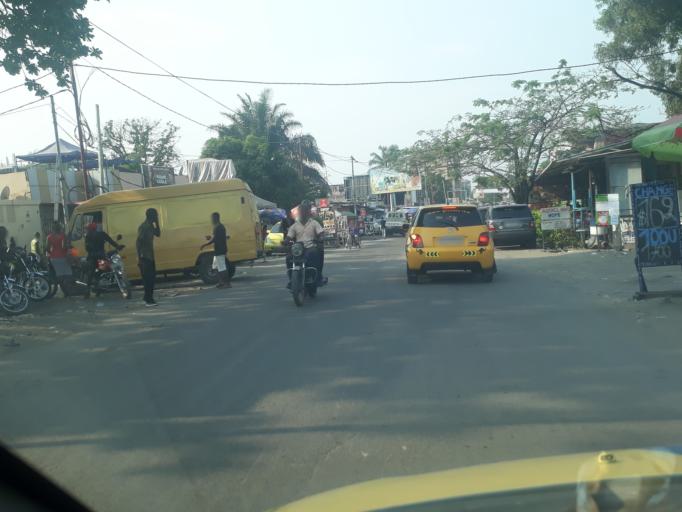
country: CD
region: Kinshasa
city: Kinshasa
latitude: -4.3201
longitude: 15.3296
